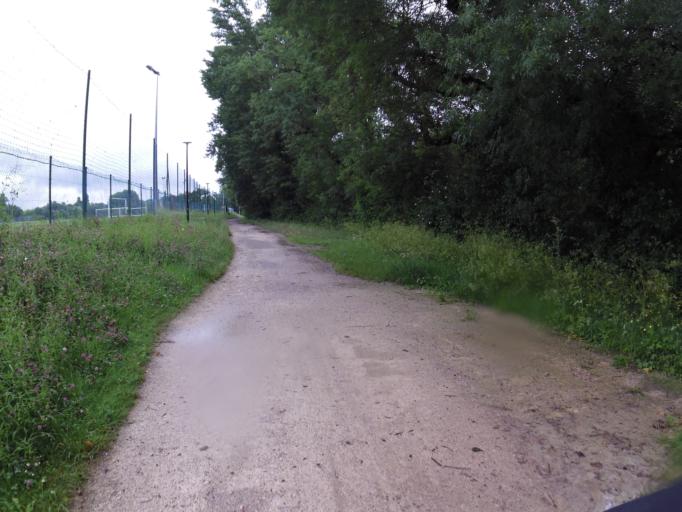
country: FR
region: Poitou-Charentes
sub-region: Departement de la Charente
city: Angouleme
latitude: 45.6557
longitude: 0.1554
